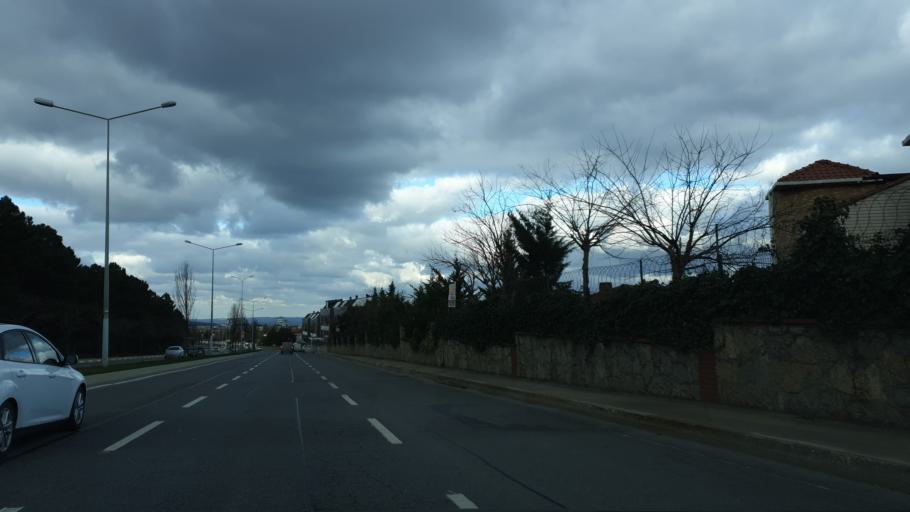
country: TR
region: Istanbul
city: Sultanbeyli
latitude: 40.9257
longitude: 29.2698
